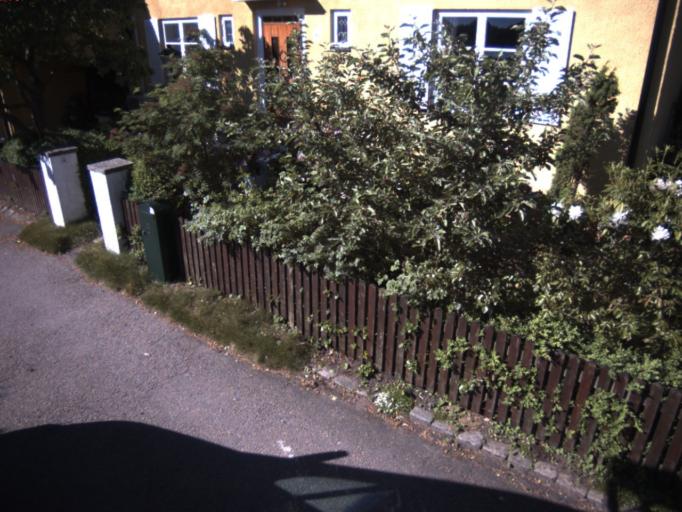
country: SE
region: Skane
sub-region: Helsingborg
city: Rydeback
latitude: 56.0001
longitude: 12.7445
